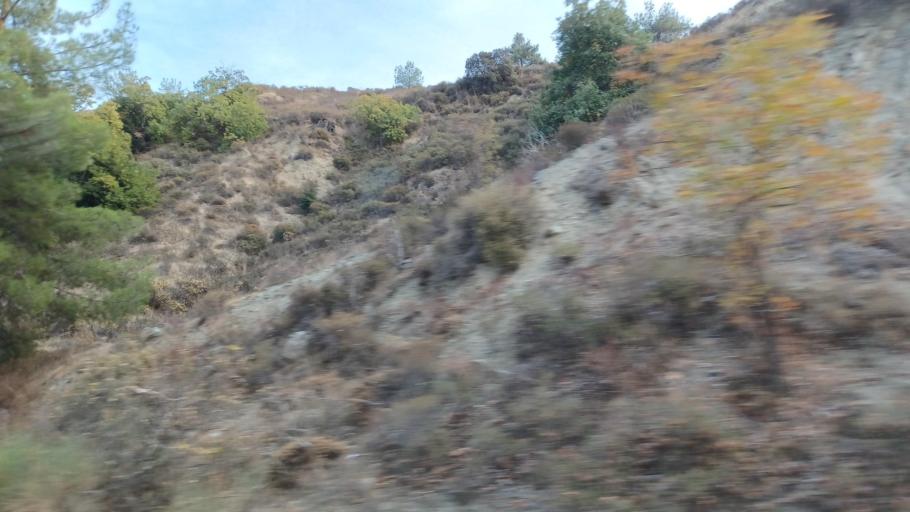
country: CY
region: Lefkosia
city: Kakopetria
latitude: 34.9899
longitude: 32.9061
